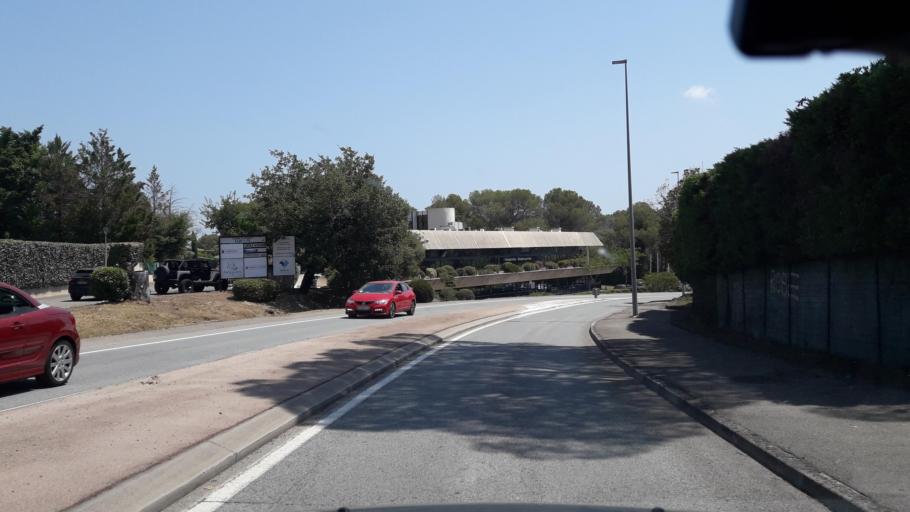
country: FR
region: Provence-Alpes-Cote d'Azur
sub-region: Departement du Var
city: Saint-Raphael
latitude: 43.4405
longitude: 6.7819
